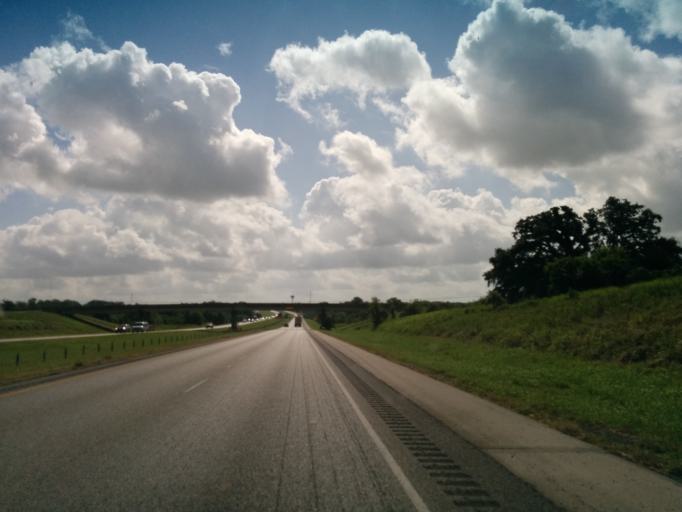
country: US
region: Texas
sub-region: Fayette County
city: Schulenburg
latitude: 29.6900
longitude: -96.9303
